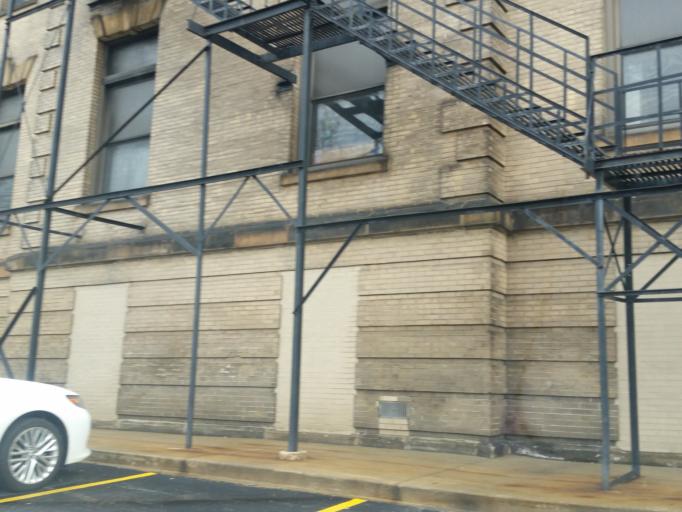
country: US
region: Ohio
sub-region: Cuyahoga County
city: Cleveland
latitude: 41.4829
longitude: -81.7120
